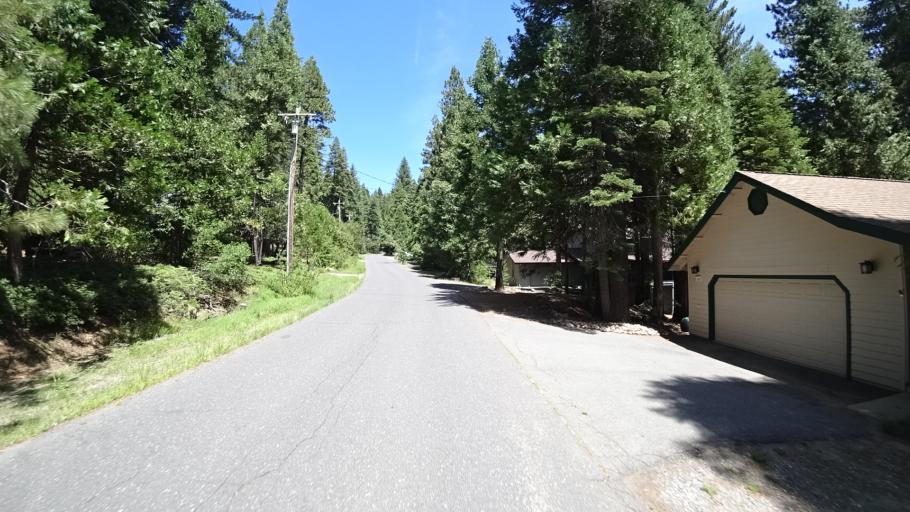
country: US
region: California
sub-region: Calaveras County
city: Arnold
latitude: 38.3106
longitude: -120.2577
